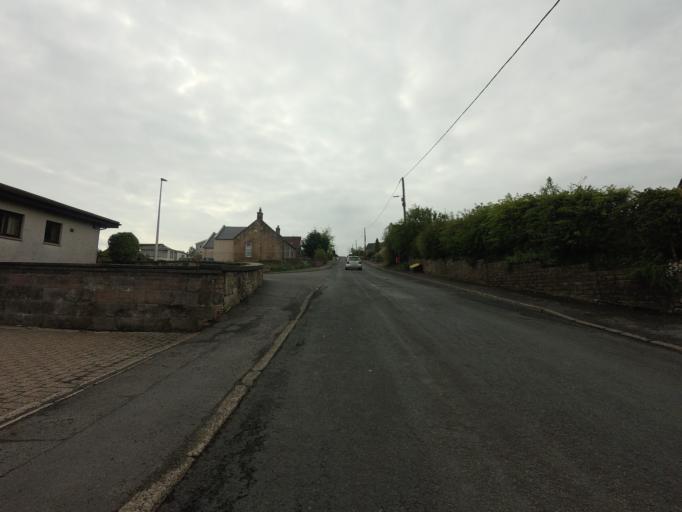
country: GB
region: Scotland
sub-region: Falkirk
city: Polmont
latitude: 55.9769
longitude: -3.7359
